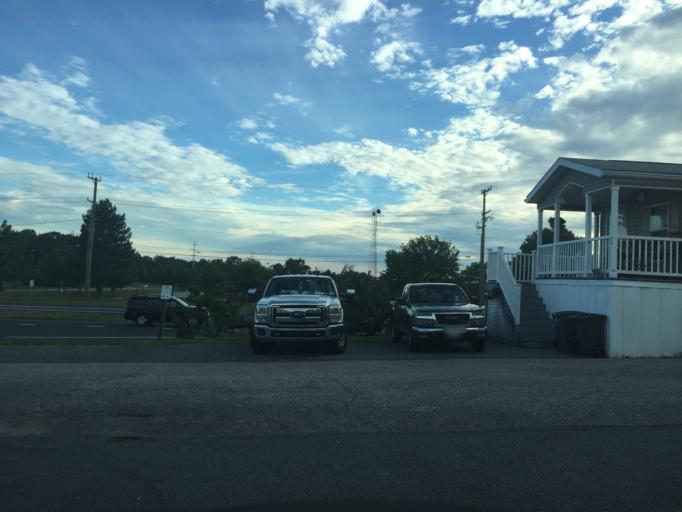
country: US
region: Maryland
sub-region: Baltimore County
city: Rossville
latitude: 39.3416
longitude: -76.4650
